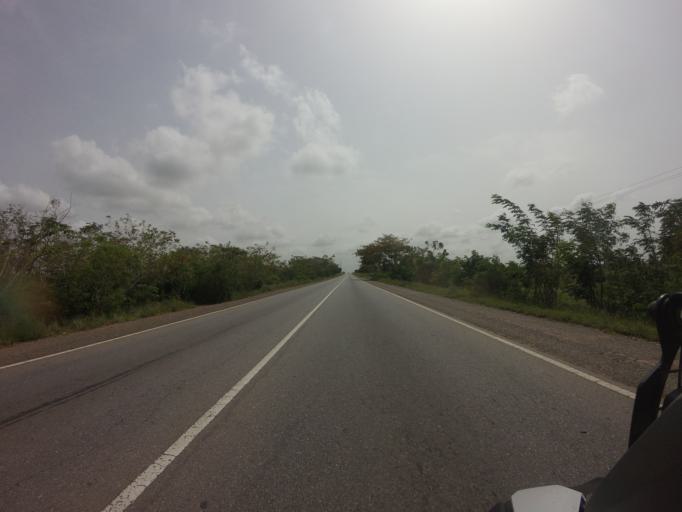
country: GH
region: Volta
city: Anloga
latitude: 5.8887
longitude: 0.4635
